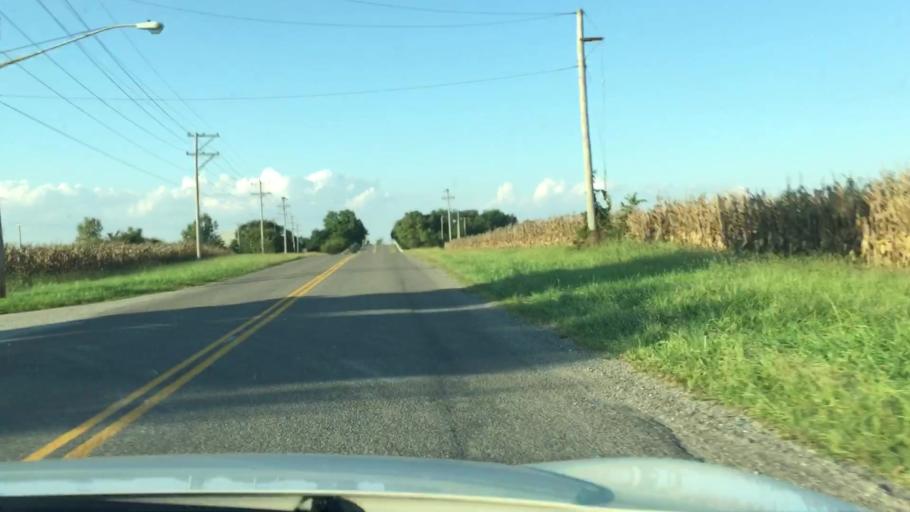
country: US
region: Ohio
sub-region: Champaign County
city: Urbana
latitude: 40.0941
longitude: -83.7715
